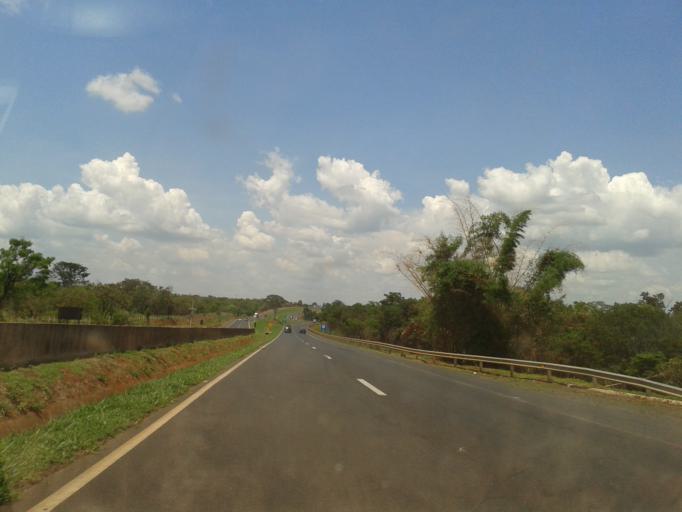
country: BR
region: Minas Gerais
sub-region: Araguari
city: Araguari
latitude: -18.6820
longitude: -48.1789
